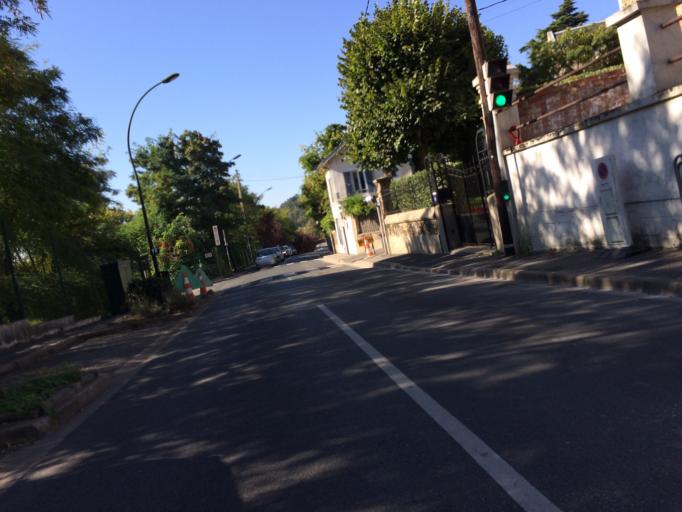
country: FR
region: Ile-de-France
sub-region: Departement de l'Essonne
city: Palaiseau
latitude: 48.7146
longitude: 2.2433
